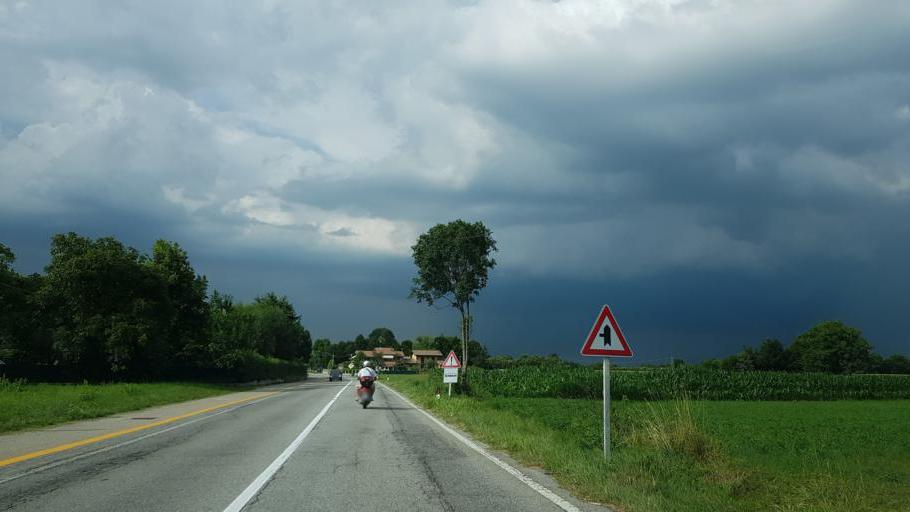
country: IT
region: Piedmont
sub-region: Provincia di Cuneo
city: Vignolo
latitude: 44.3674
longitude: 7.4740
